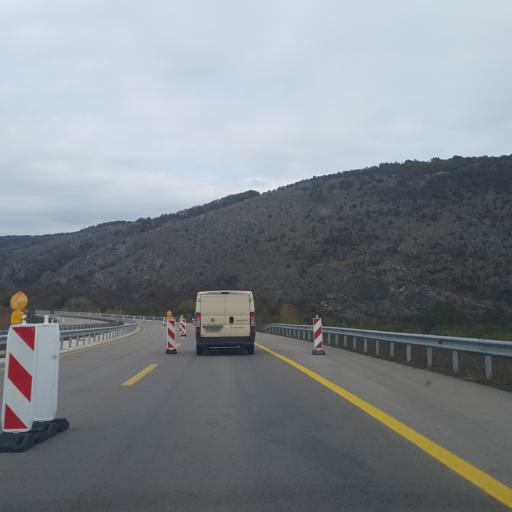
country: RS
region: Central Serbia
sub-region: Pirotski Okrug
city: Bela Palanka
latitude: 43.2317
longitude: 22.3794
